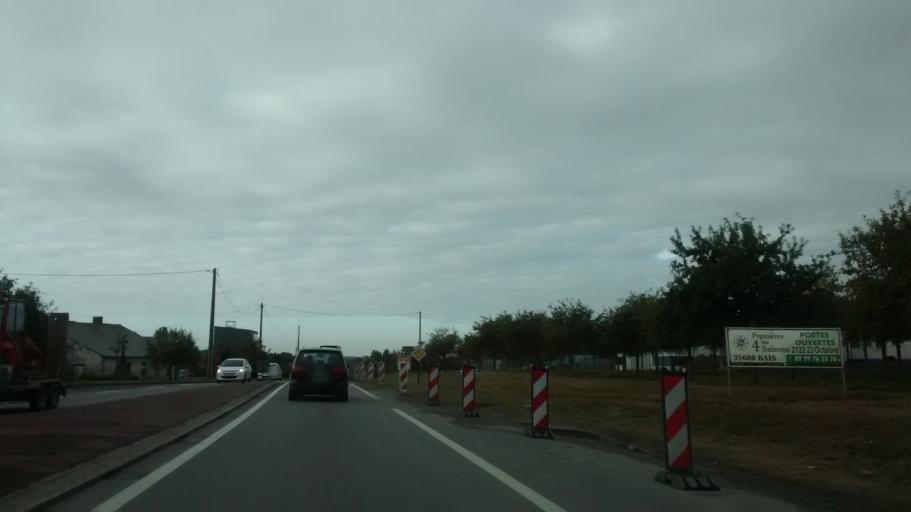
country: FR
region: Brittany
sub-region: Departement d'Ille-et-Vilaine
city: Torce
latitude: 48.0778
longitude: -1.2638
